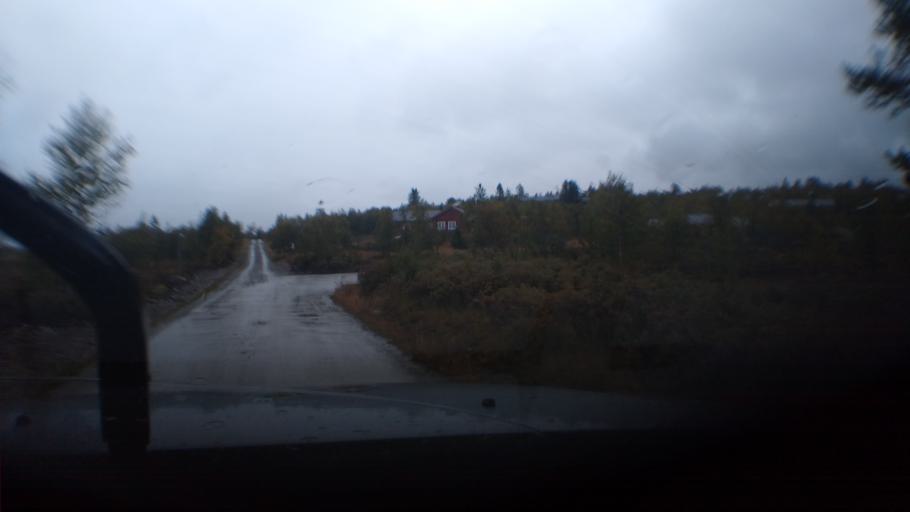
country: NO
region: Oppland
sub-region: Ringebu
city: Ringebu
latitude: 61.6509
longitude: 10.0959
